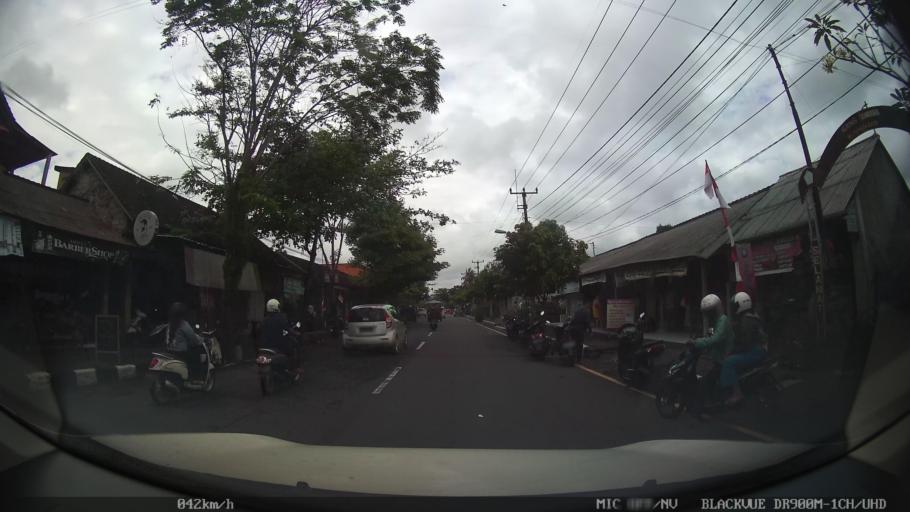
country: ID
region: Bali
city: Banjar Serangan
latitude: -8.5467
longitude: 115.1699
